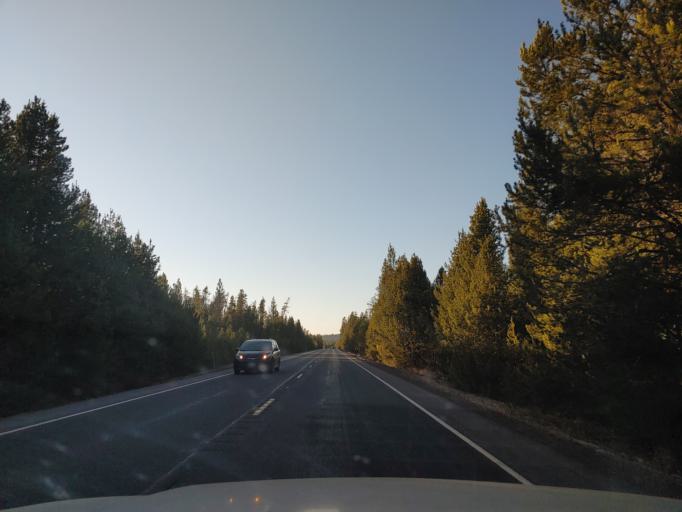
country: US
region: Oregon
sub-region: Deschutes County
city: La Pine
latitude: 43.4111
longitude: -121.8317
